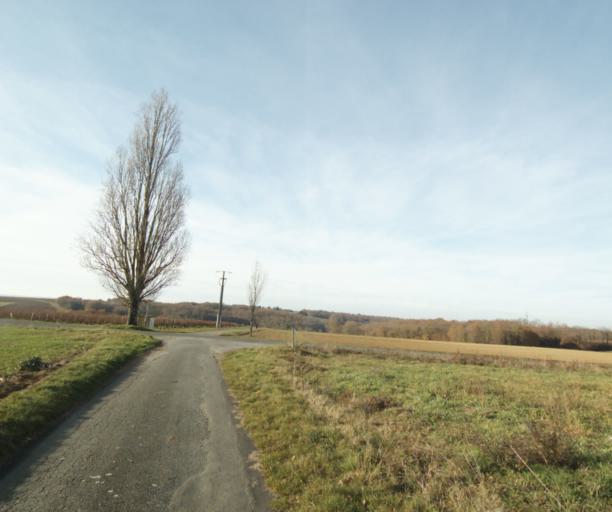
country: FR
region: Poitou-Charentes
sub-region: Departement de la Charente-Maritime
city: Chaniers
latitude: 45.7241
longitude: -0.5273
